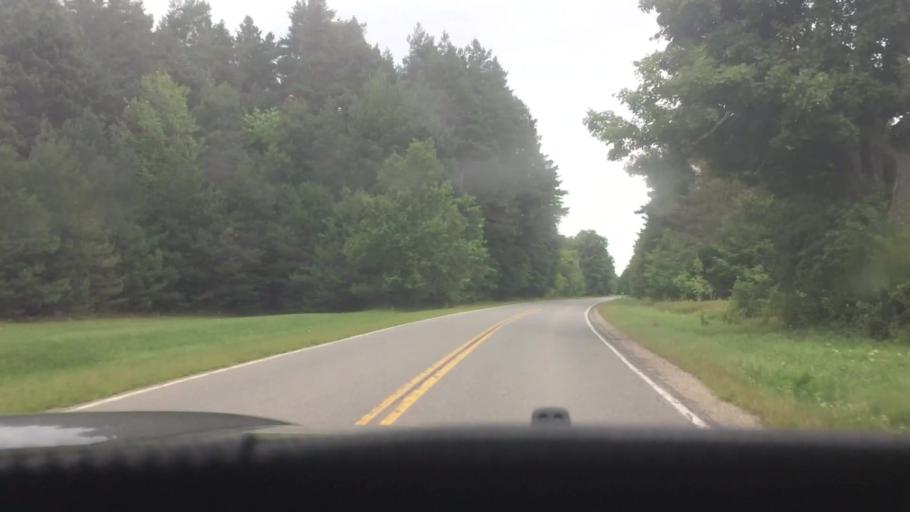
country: US
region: New York
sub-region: St. Lawrence County
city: Hannawa Falls
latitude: 44.5973
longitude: -74.8874
